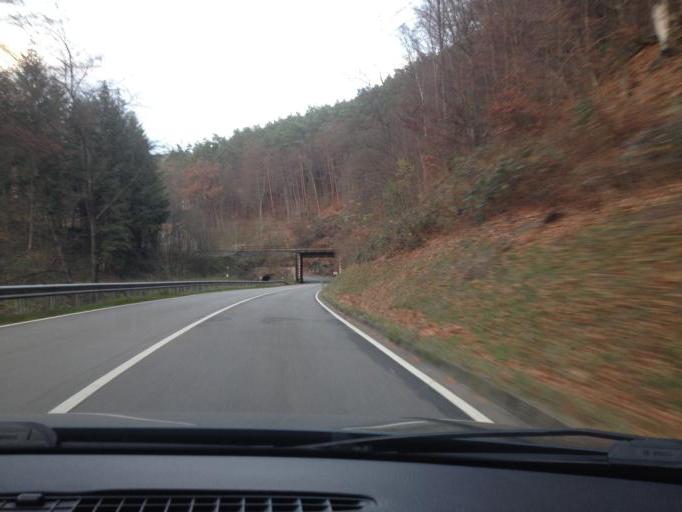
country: DE
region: Rheinland-Pfalz
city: Weidenthal
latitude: 49.4104
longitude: 8.0065
